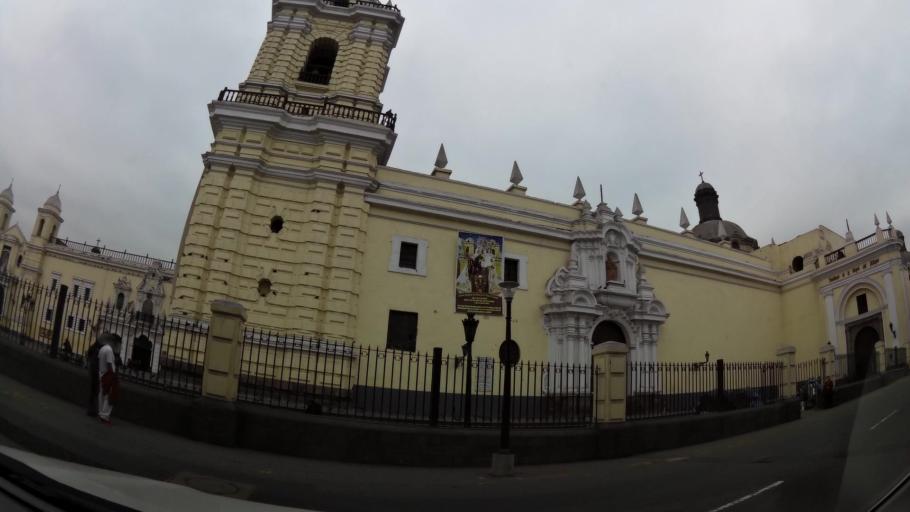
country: PE
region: Lima
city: Lima
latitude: -12.0458
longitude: -77.0276
